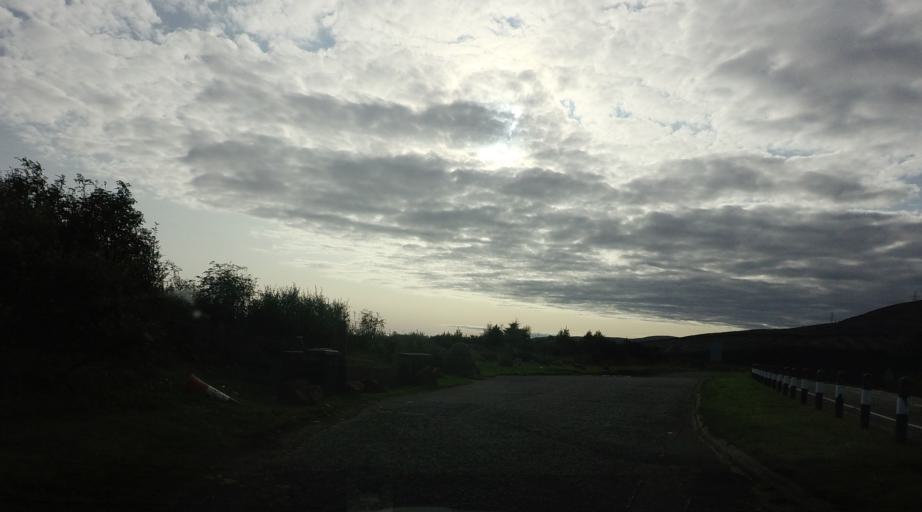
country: GB
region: Scotland
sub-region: Highland
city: Brora
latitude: 58.1407
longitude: -3.6027
